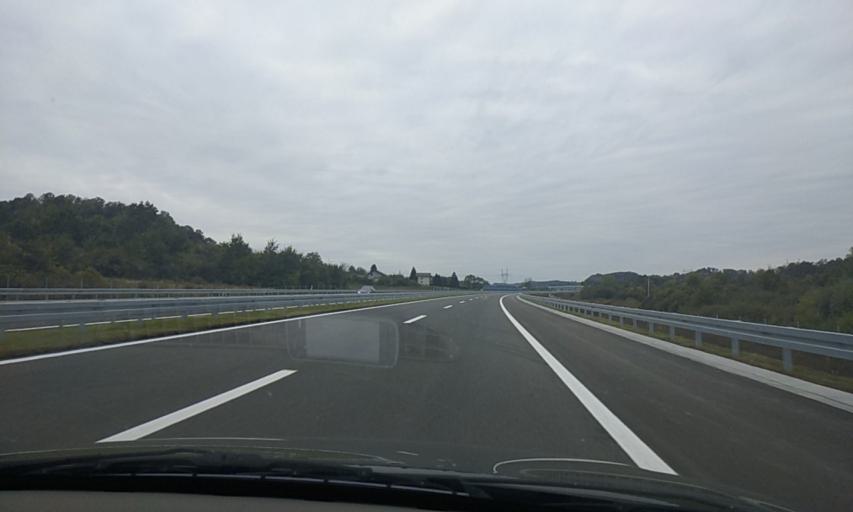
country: BA
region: Republika Srpska
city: Prnjavor
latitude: 44.8911
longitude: 17.5814
